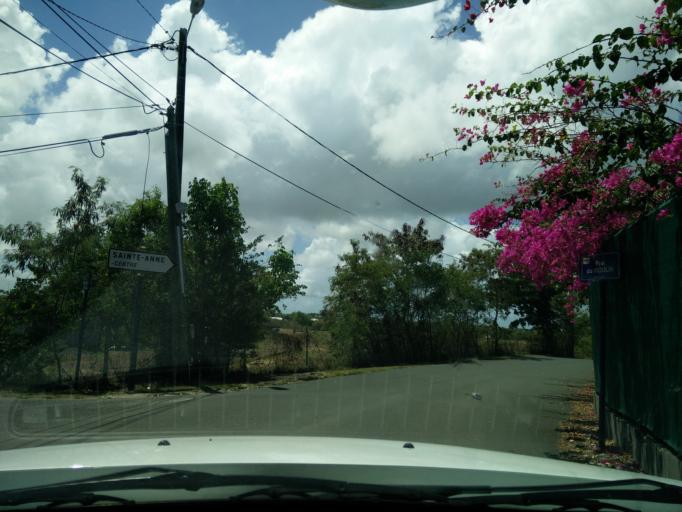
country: GP
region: Guadeloupe
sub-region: Guadeloupe
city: Sainte-Anne
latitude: 16.2472
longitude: -61.3450
